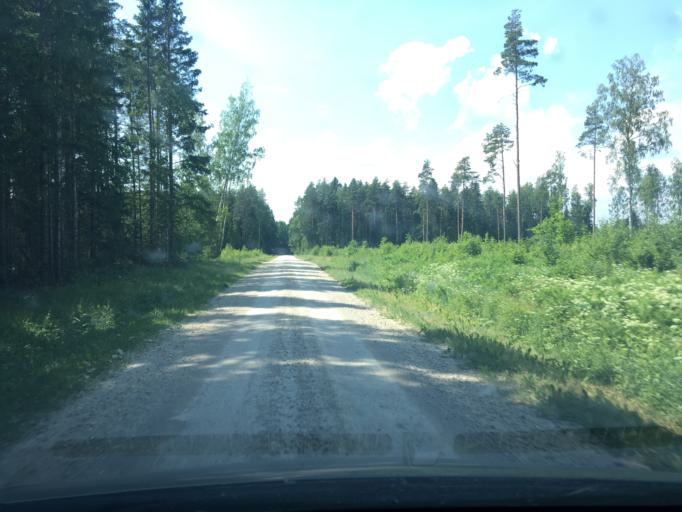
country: EE
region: Raplamaa
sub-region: Maerjamaa vald
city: Marjamaa
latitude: 58.8063
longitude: 24.4247
